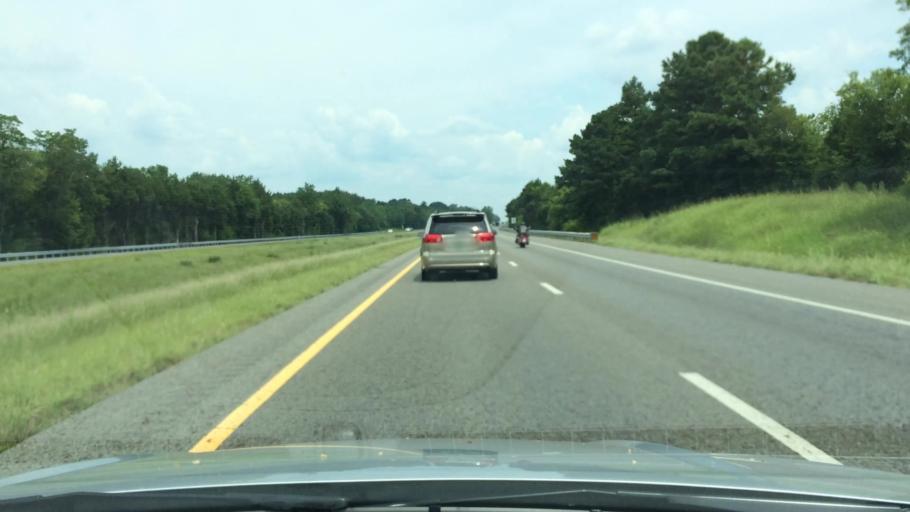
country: US
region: Tennessee
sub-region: Marshall County
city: Lewisburg
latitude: 35.4559
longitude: -86.8854
